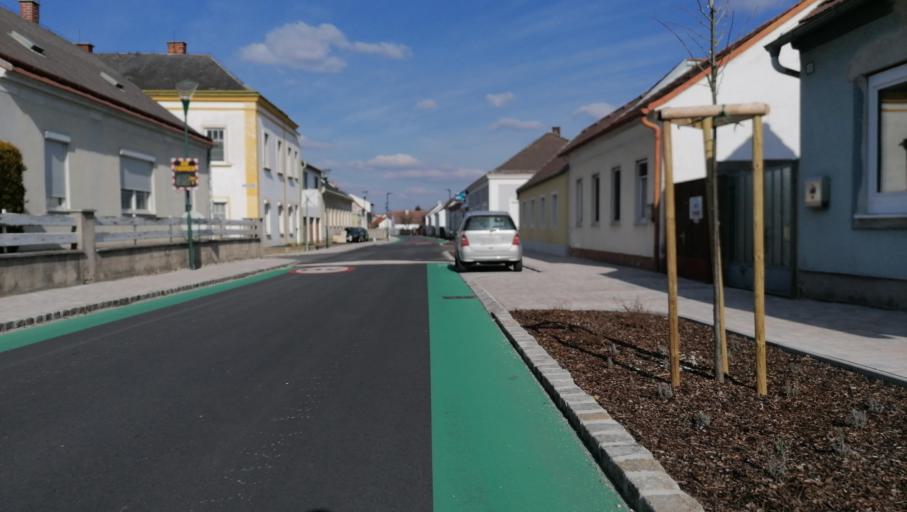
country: AT
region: Lower Austria
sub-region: Politischer Bezirk Wiener Neustadt
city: Lichtenworth
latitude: 47.8332
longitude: 16.2894
